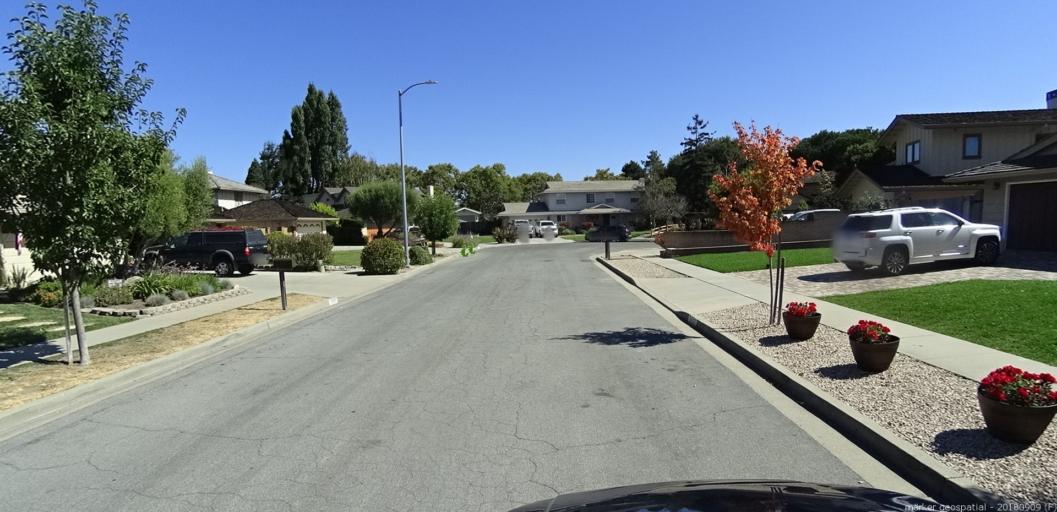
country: US
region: California
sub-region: Monterey County
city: Carmel Valley Village
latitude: 36.5914
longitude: -121.7106
